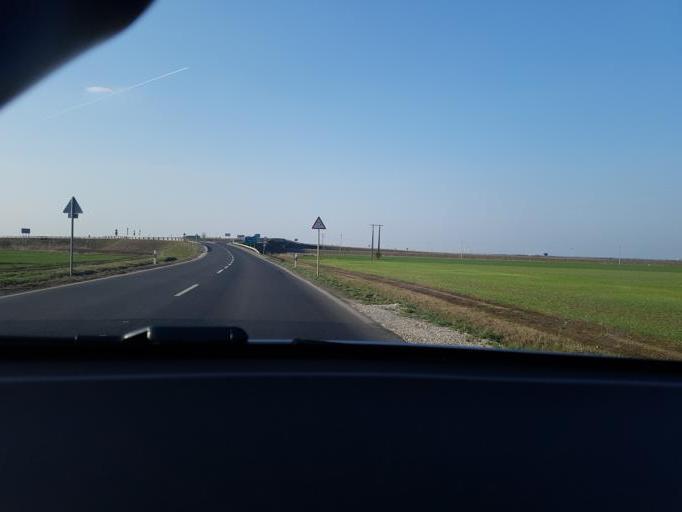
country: HU
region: Csongrad
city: Csanadpalota
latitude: 46.2128
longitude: 20.7164
